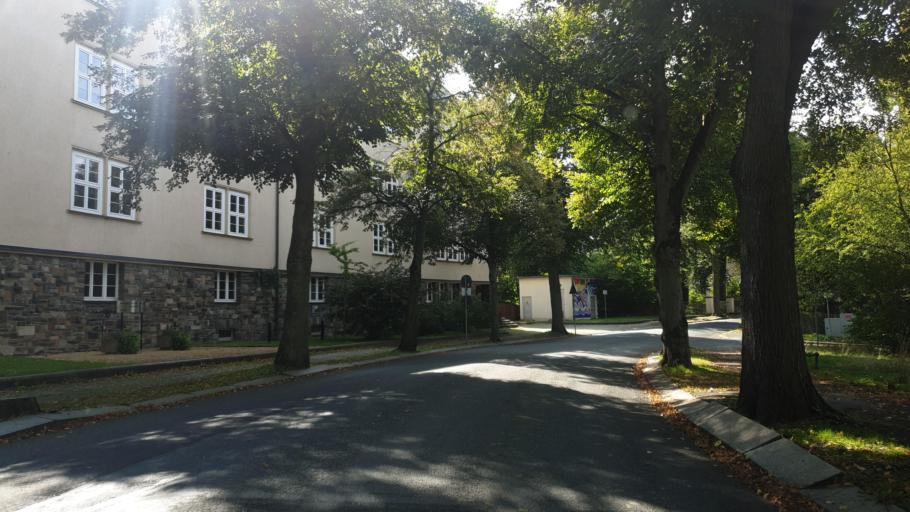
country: DE
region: Saxony
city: Rodewisch
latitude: 50.5297
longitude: 12.4102
